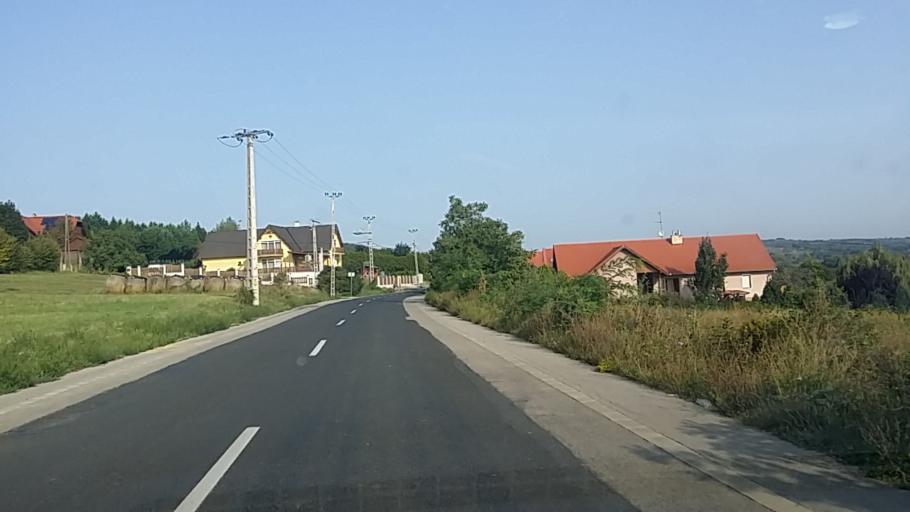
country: HU
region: Gyor-Moson-Sopron
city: Nagycenk
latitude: 47.6422
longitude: 16.6730
